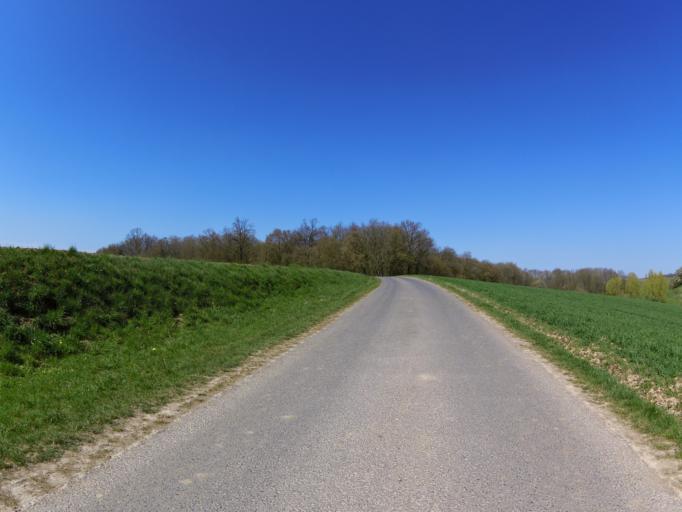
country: DE
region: Bavaria
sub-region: Regierungsbezirk Unterfranken
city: Rottendorf
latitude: 49.8226
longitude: 10.0503
